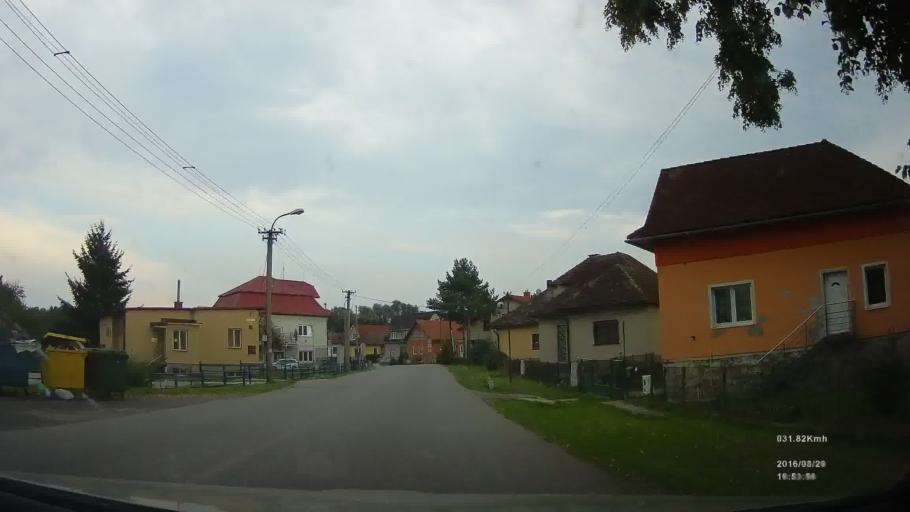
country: SK
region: Zilinsky
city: Ruzomberok
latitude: 49.0988
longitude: 19.4115
